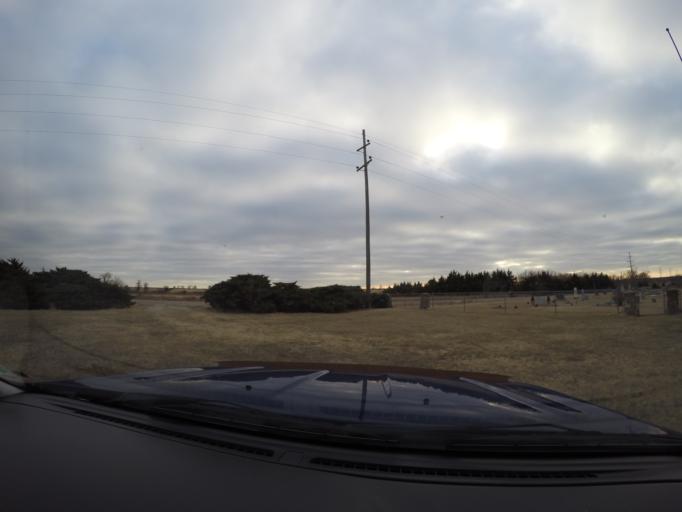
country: US
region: Kansas
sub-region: Morris County
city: Council Grove
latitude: 38.8846
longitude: -96.5345
